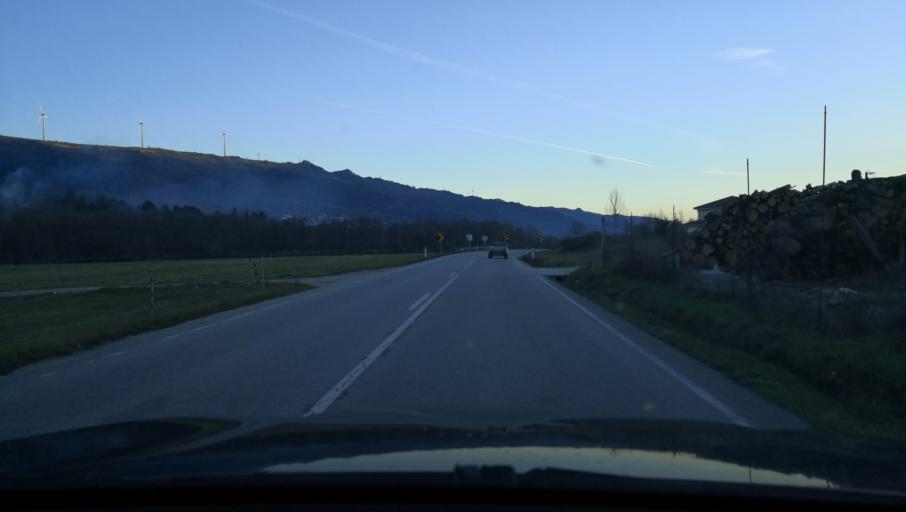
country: PT
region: Vila Real
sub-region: Vila Pouca de Aguiar
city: Vila Pouca de Aguiar
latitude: 41.4604
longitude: -7.6651
